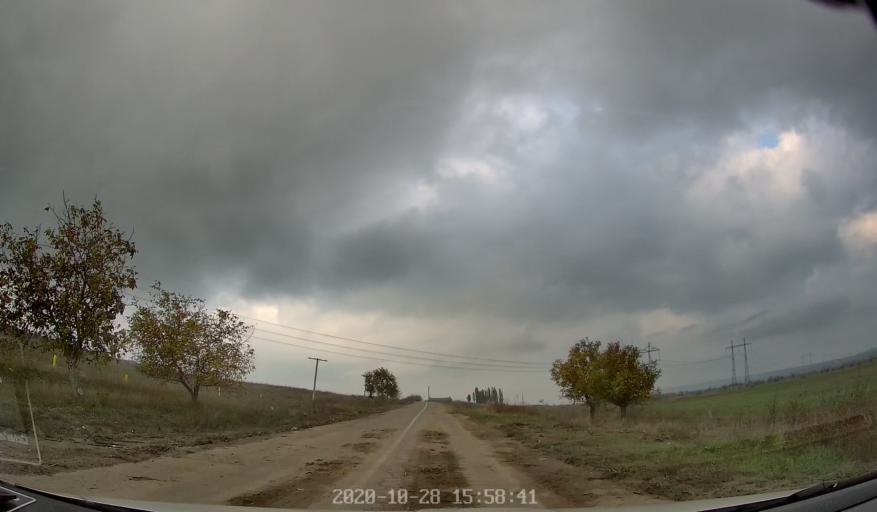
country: UA
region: Odessa
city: Zaliznychne
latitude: 45.7677
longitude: 28.5719
